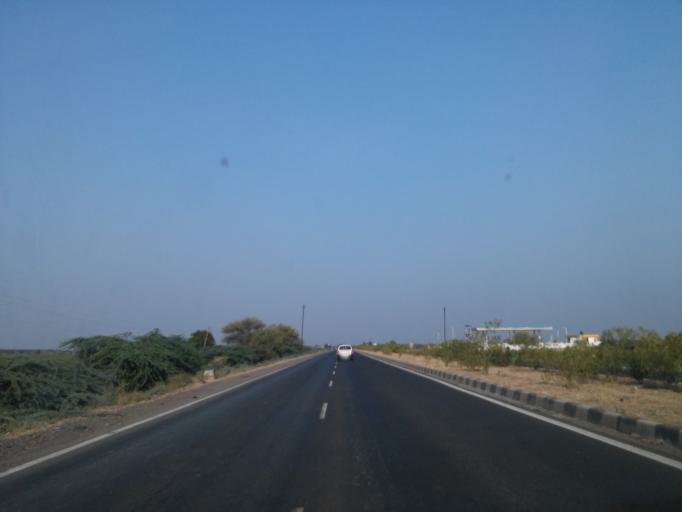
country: IN
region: Gujarat
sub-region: Surendranagar
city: Lakhtar
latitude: 23.0530
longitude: 71.7166
